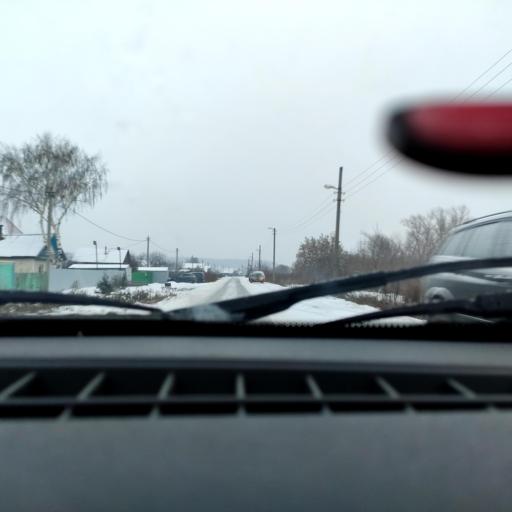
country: RU
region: Bashkortostan
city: Blagoveshchensk
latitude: 54.8989
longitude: 56.0197
